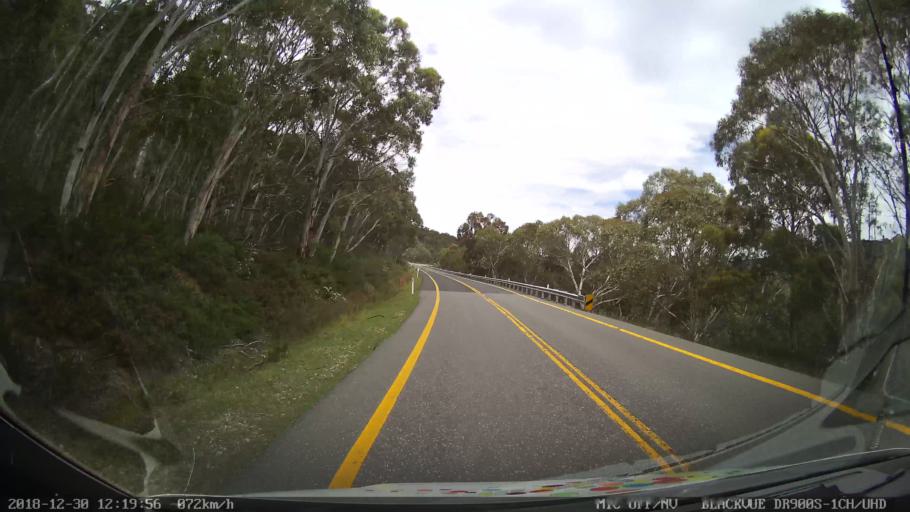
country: AU
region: New South Wales
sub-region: Snowy River
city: Jindabyne
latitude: -36.3447
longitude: 148.5358
